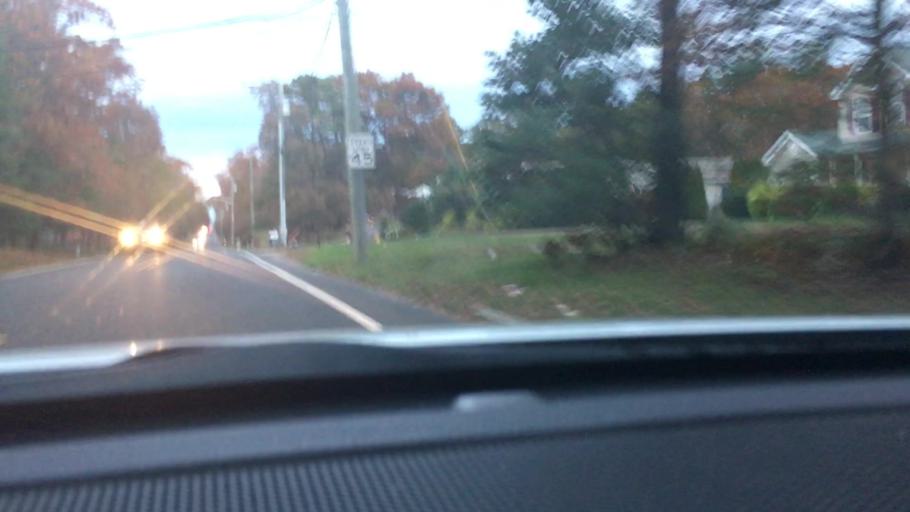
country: US
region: New Jersey
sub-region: Atlantic County
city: Absecon
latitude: 39.4439
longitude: -74.4973
